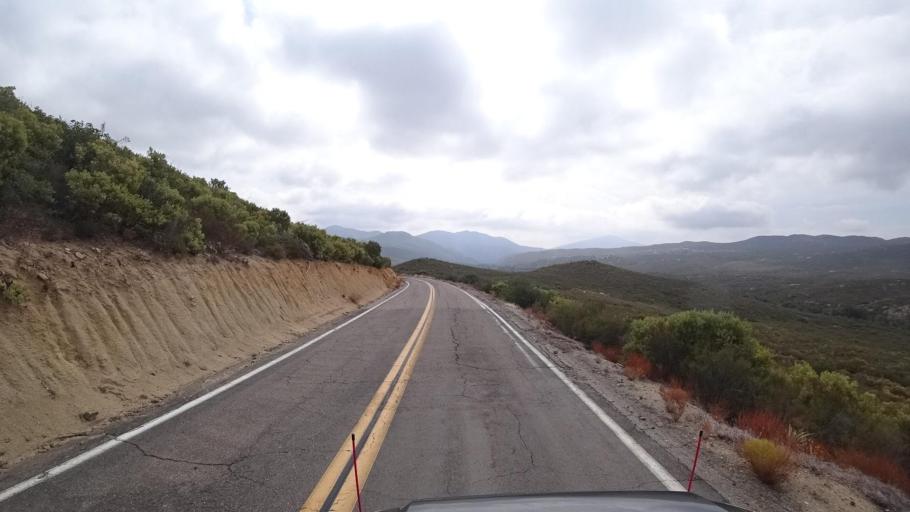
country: US
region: California
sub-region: San Diego County
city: Descanso
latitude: 32.9119
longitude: -116.6436
